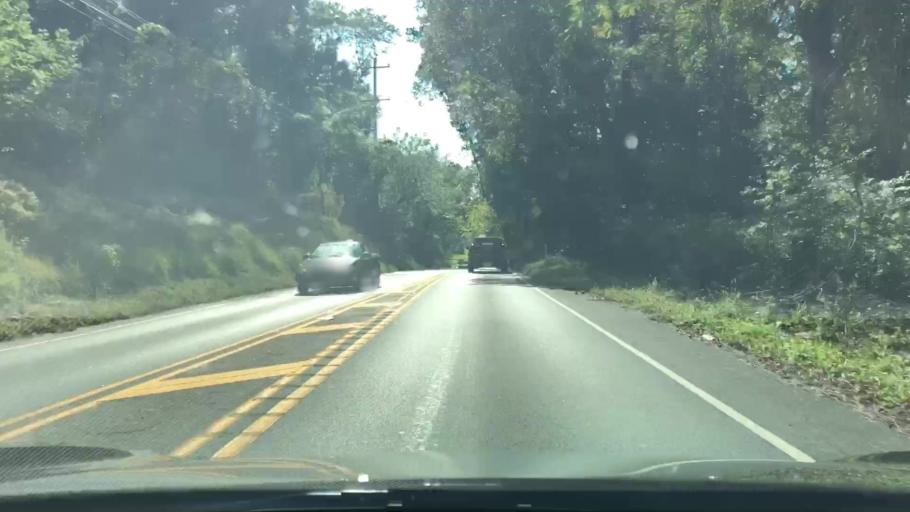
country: US
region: Pennsylvania
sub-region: Chester County
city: West Chester
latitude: 39.9240
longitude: -75.5680
